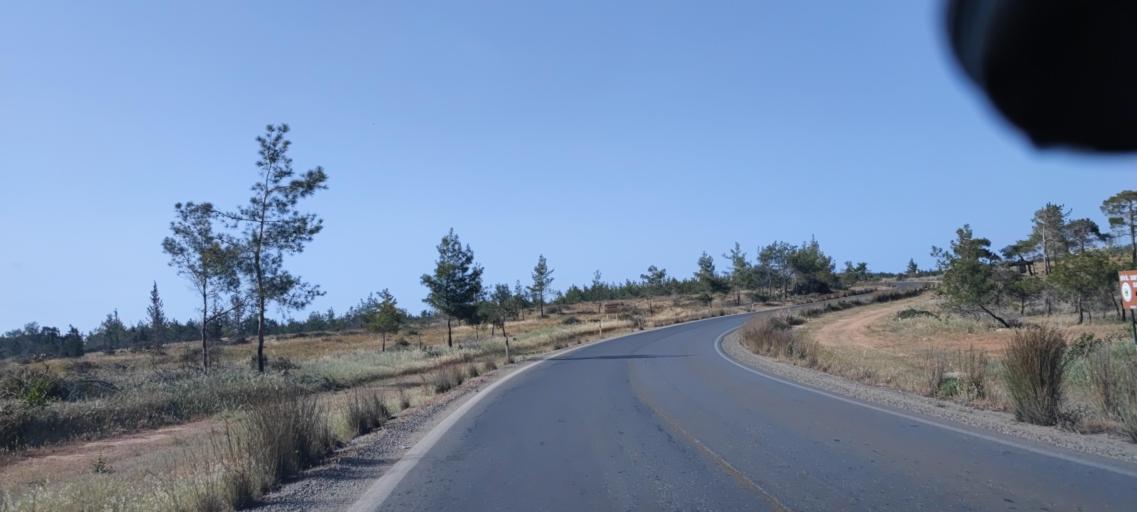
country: CY
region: Lefkosia
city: Morfou
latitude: 35.2799
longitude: 33.0405
